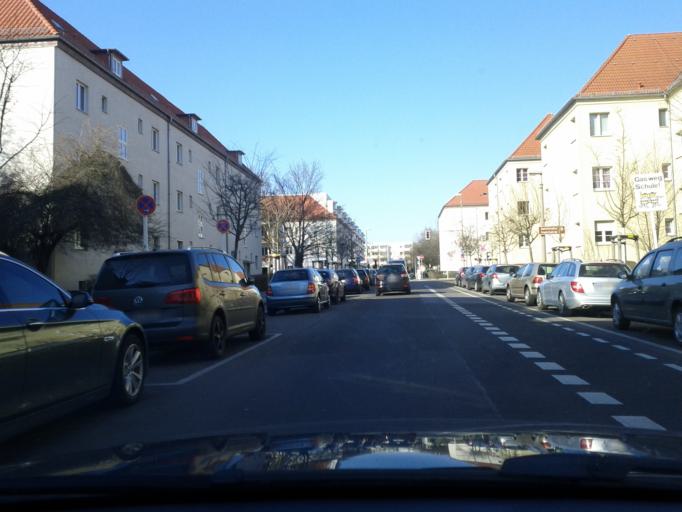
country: DE
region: Berlin
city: Lichtenberg
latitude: 52.5154
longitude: 13.4934
